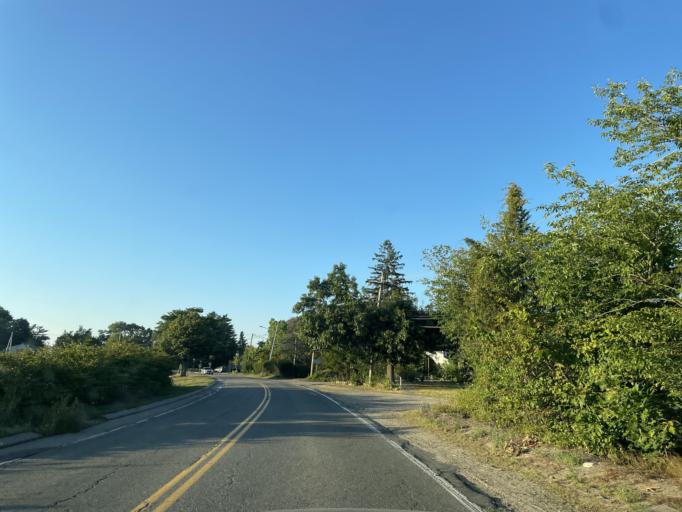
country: US
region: Massachusetts
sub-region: Plymouth County
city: Hanson
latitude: 42.0571
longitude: -70.8354
